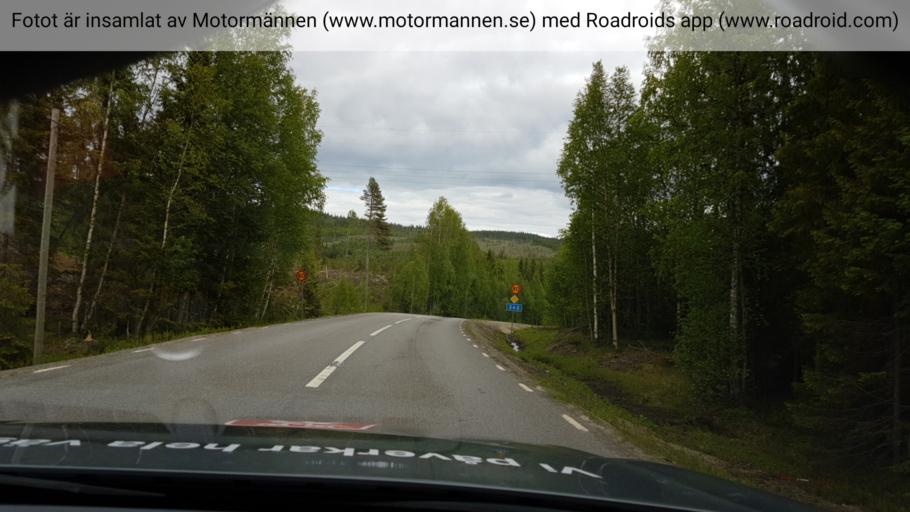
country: SE
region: Jaemtland
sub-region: Stroemsunds Kommun
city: Stroemsund
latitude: 64.3454
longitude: 14.8144
